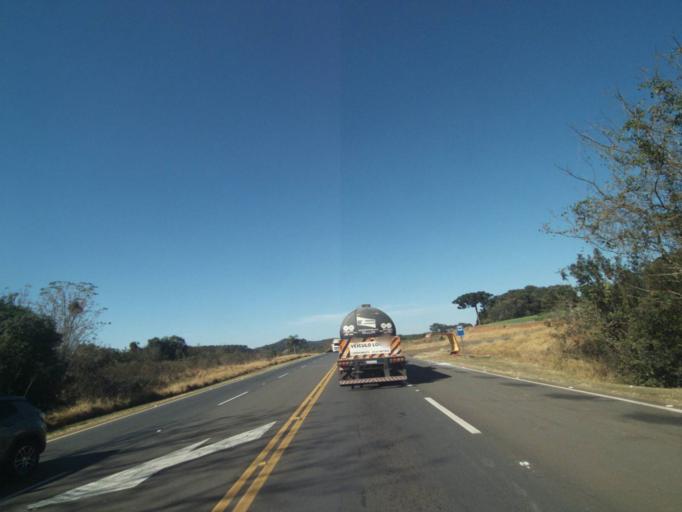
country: BR
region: Parana
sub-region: Tibagi
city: Tibagi
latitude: -24.7041
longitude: -50.5584
